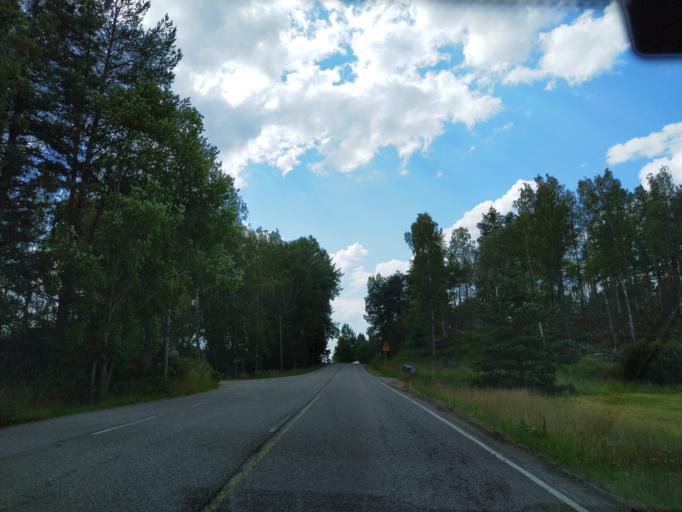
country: FI
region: Uusimaa
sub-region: Helsinki
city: Kirkkonummi
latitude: 60.0854
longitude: 24.5007
